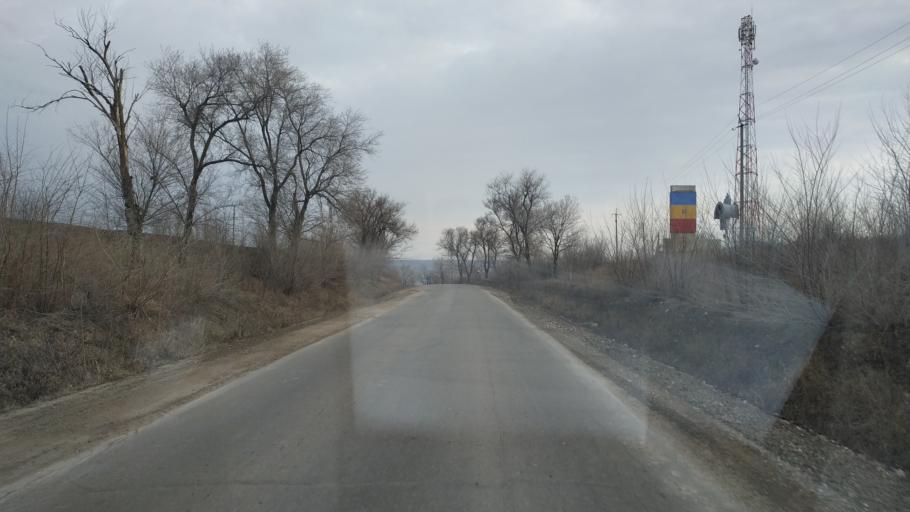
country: MD
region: Chisinau
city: Singera
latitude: 46.9495
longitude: 29.0564
